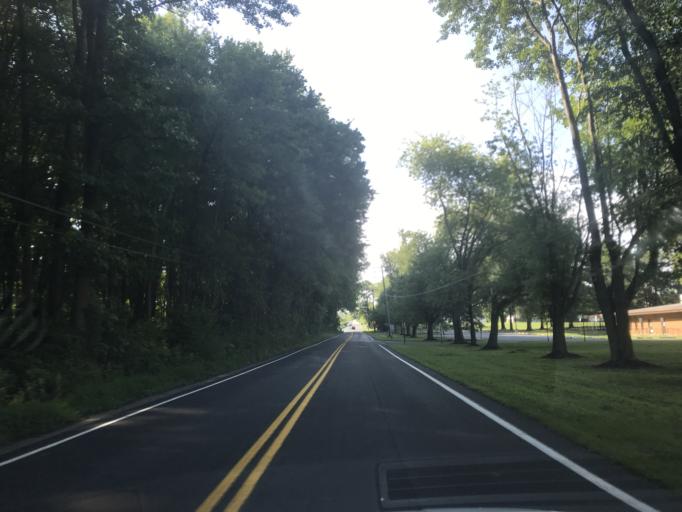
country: US
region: Maryland
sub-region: Harford County
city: Aberdeen
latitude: 39.5212
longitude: -76.1363
